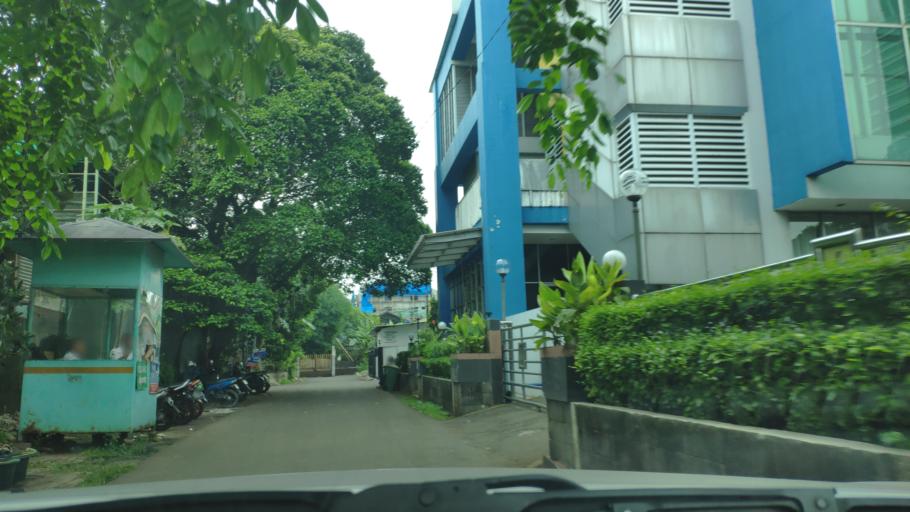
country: ID
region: Jakarta Raya
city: Jakarta
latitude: -6.1943
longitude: 106.7970
